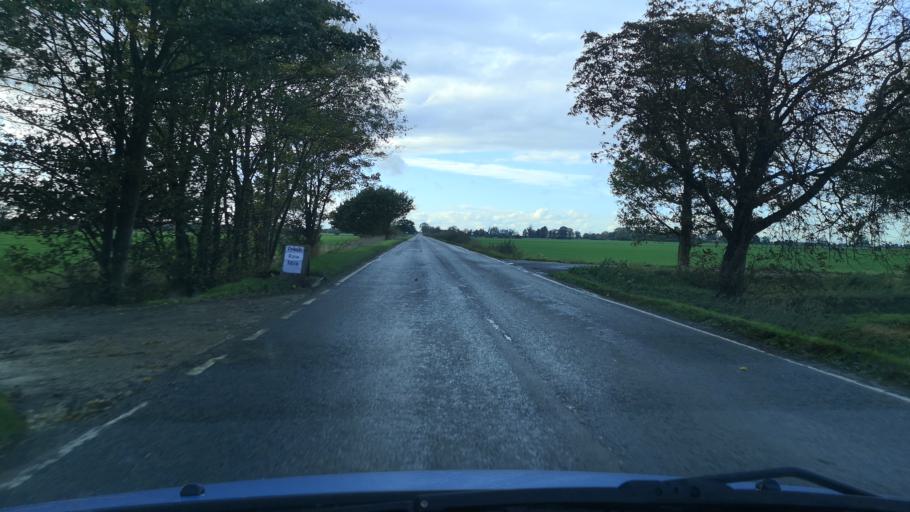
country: GB
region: England
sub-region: North Lincolnshire
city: Crowle
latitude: 53.5844
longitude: -0.9035
